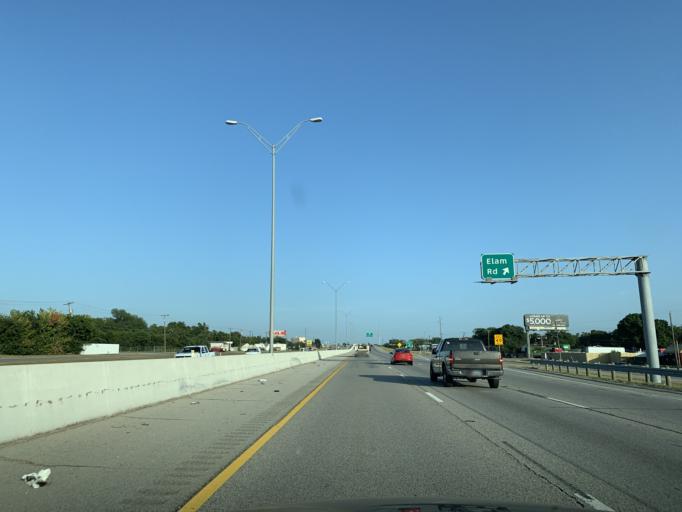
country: US
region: Texas
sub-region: Dallas County
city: Hutchins
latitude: 32.7227
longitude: -96.6978
